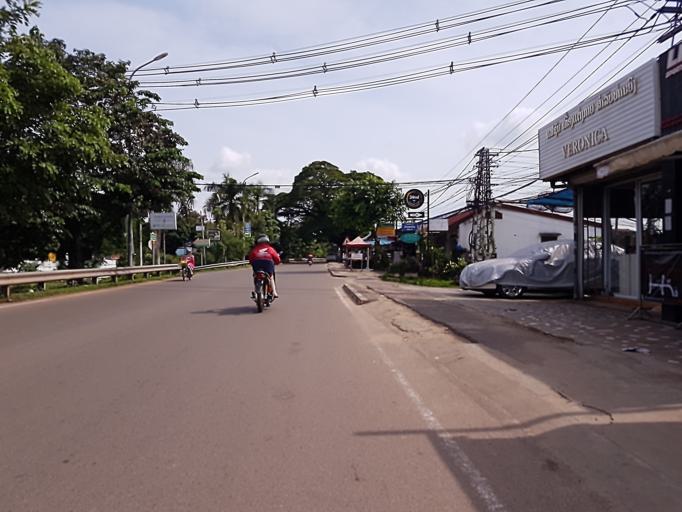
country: LA
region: Vientiane
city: Vientiane
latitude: 17.9537
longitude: 102.6224
